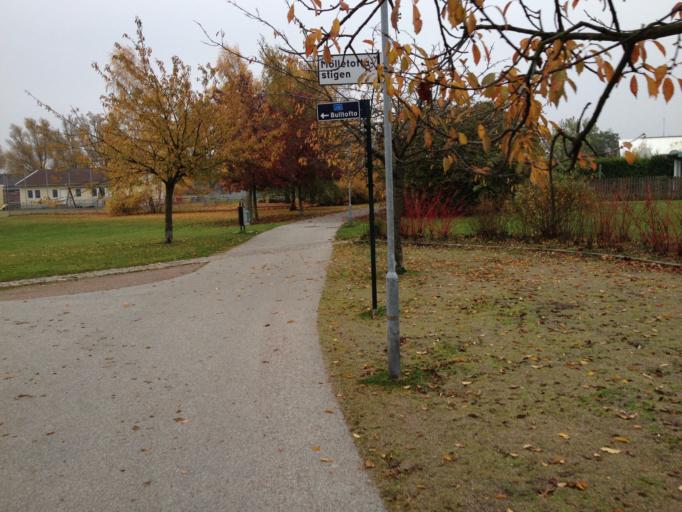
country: SE
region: Skane
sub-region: Burlovs Kommun
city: Arloev
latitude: 55.6039
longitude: 13.0524
